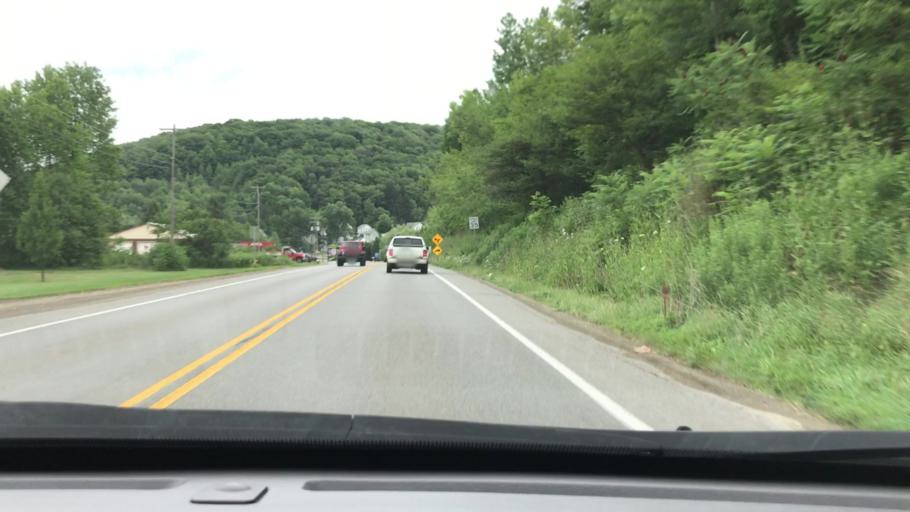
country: US
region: Pennsylvania
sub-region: Elk County
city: Johnsonburg
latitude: 41.4763
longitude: -78.6702
